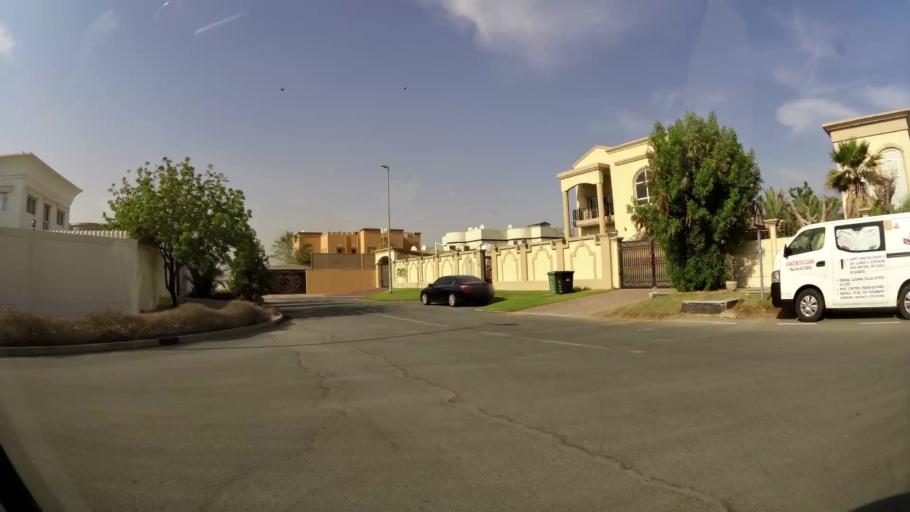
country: AE
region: Ash Shariqah
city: Sharjah
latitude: 25.2410
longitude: 55.4092
